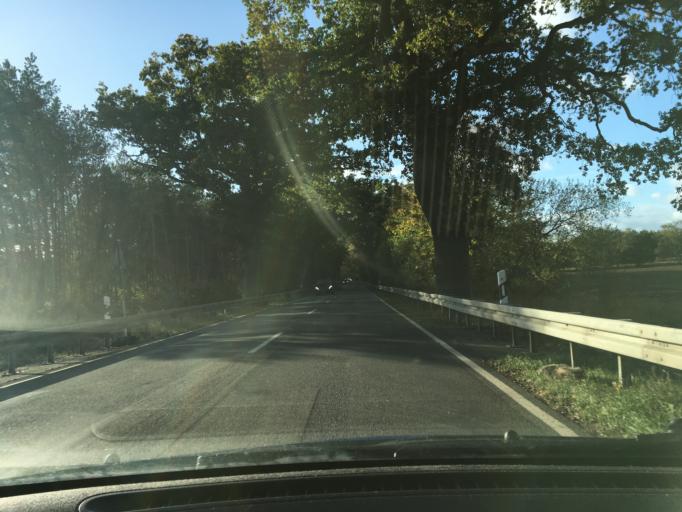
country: DE
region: Mecklenburg-Vorpommern
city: Boizenburg
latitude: 53.3871
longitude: 10.8396
